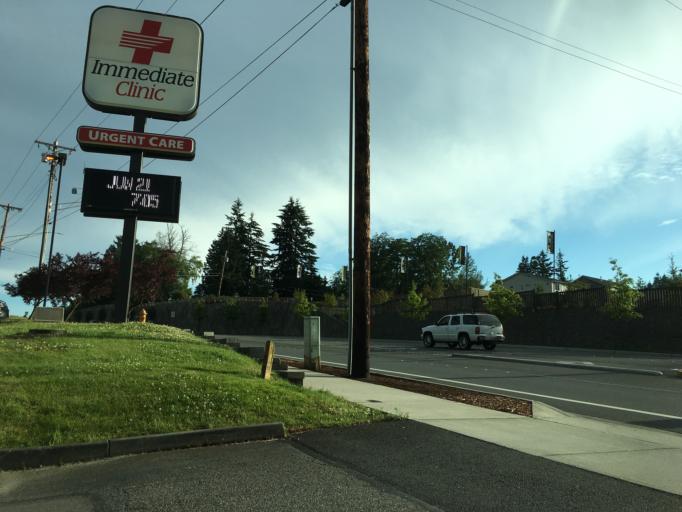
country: US
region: Washington
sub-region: King County
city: Bothell
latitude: 47.7884
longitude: -122.2190
